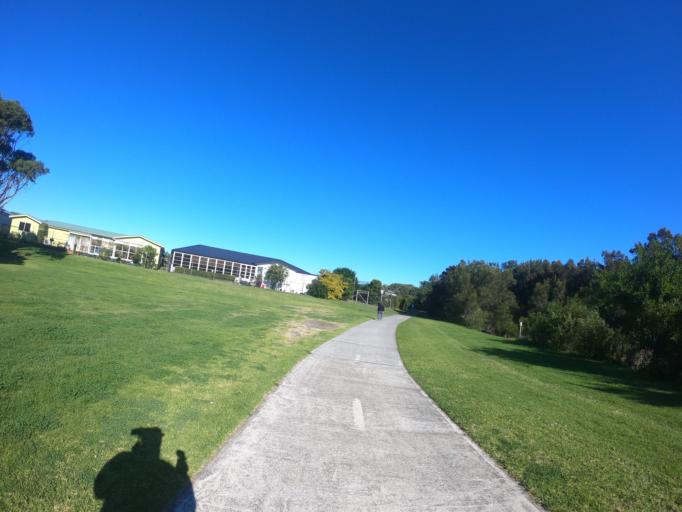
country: AU
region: New South Wales
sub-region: Wollongong
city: Corrimal
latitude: -34.3883
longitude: 150.9090
